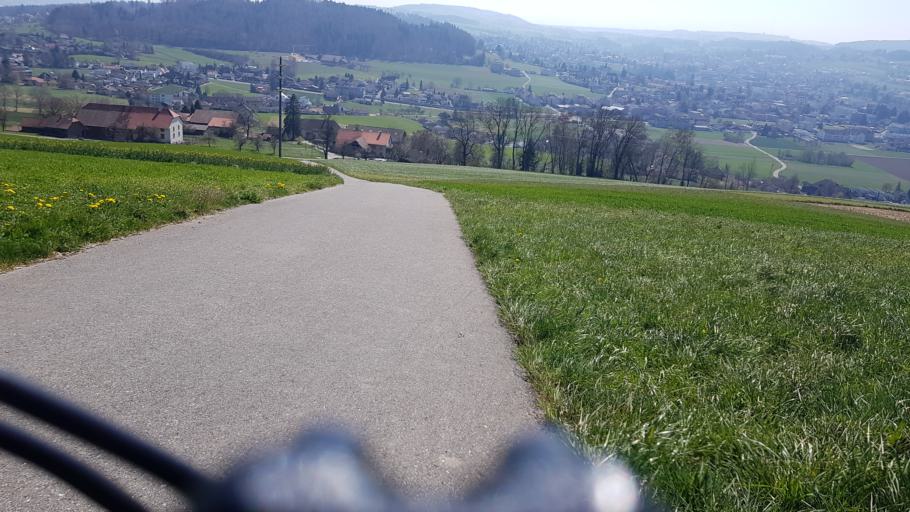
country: CH
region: Aargau
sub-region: Bezirk Kulm
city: Reinach
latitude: 47.2702
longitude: 8.1864
